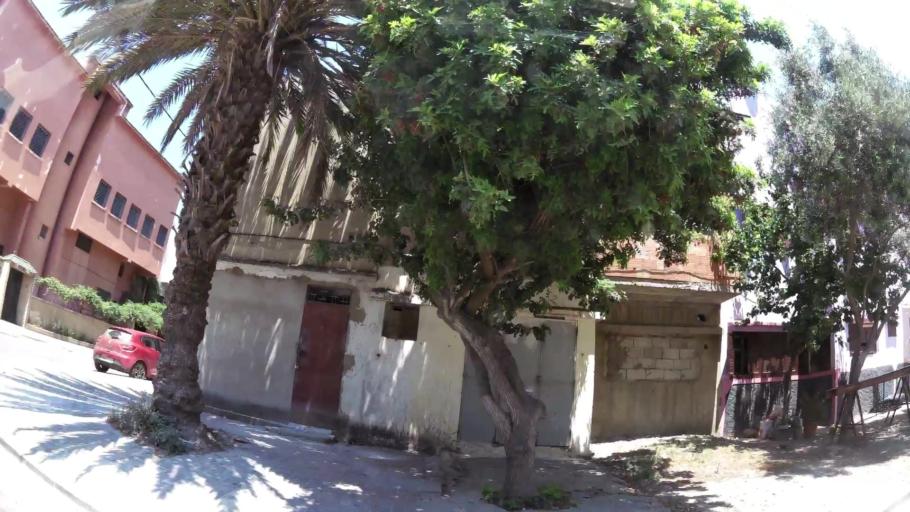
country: MA
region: Rabat-Sale-Zemmour-Zaer
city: Sale
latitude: 34.0650
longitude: -6.7930
